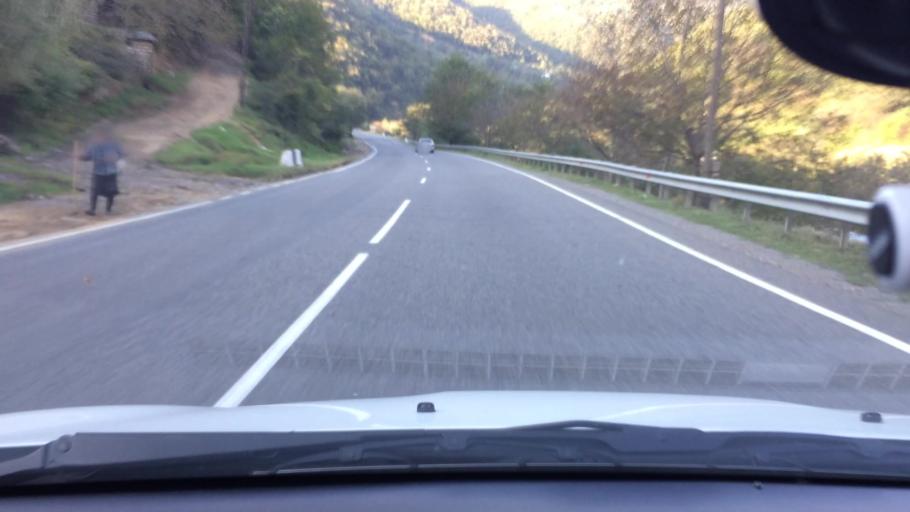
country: GE
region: Imereti
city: Kharagauli
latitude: 42.1091
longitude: 43.3571
